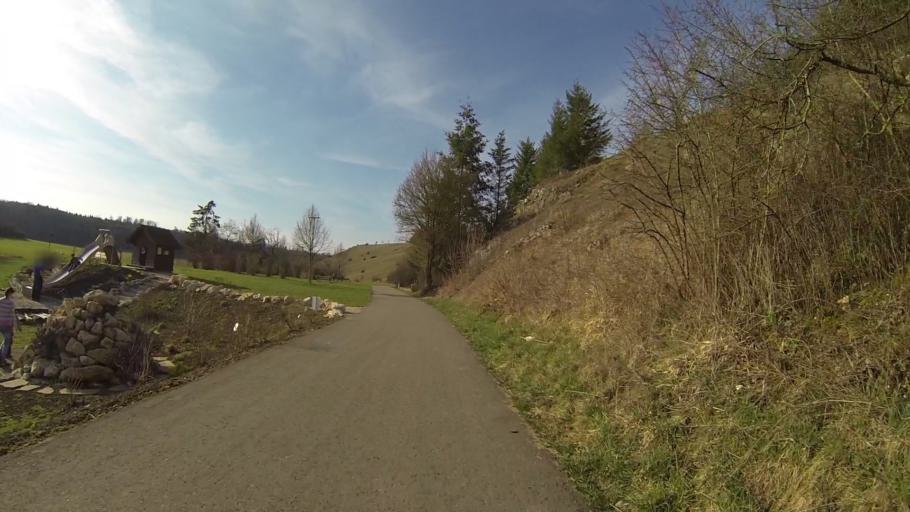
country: DE
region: Baden-Wuerttemberg
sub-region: Regierungsbezirk Stuttgart
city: Hermaringen
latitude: 48.5835
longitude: 10.2273
